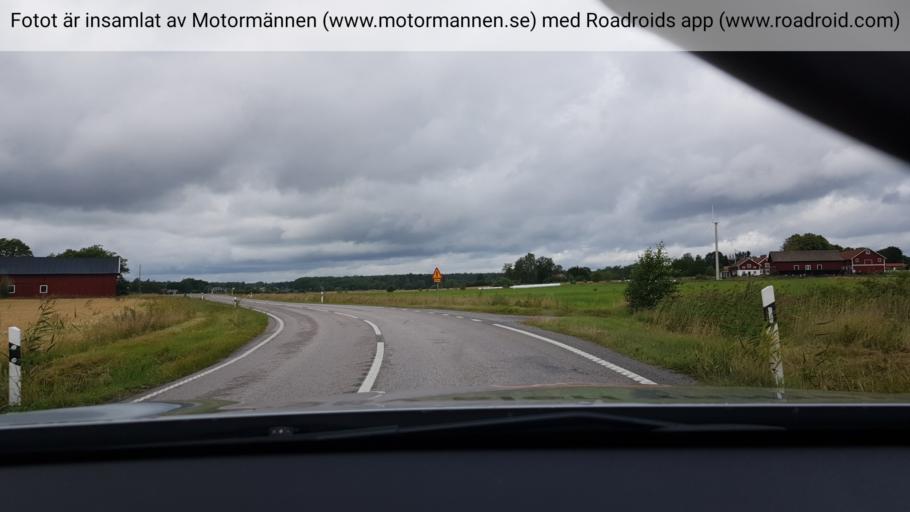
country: SE
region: Stockholm
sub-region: Norrtalje Kommun
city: Rimbo
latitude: 59.7411
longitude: 18.3969
